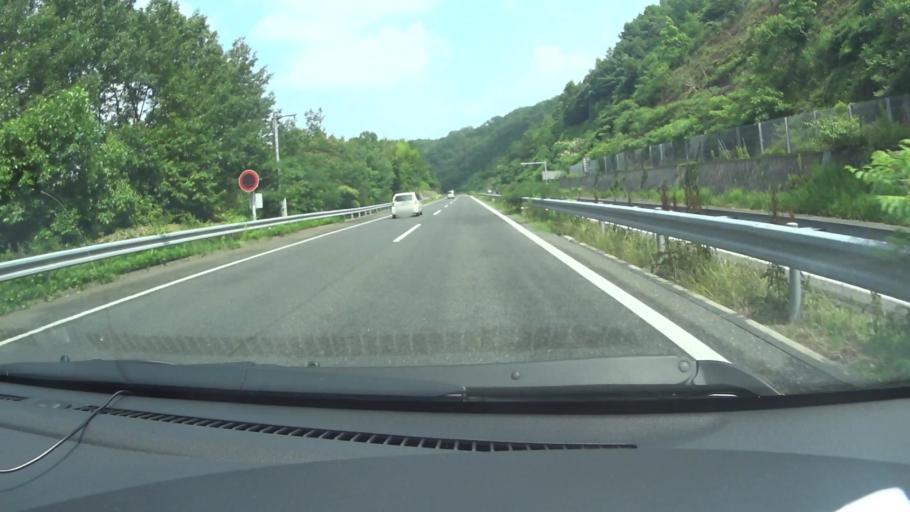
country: JP
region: Kyoto
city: Kameoka
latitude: 35.0975
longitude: 135.4965
